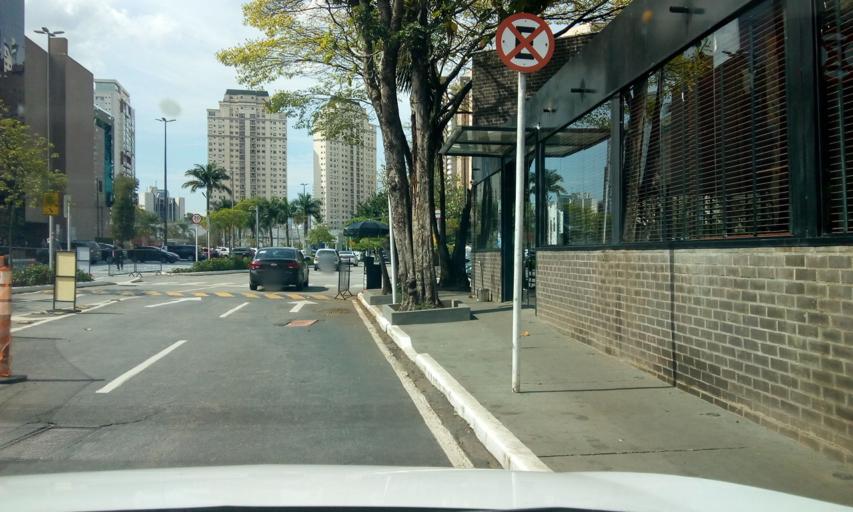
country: BR
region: Sao Paulo
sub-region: Taboao Da Serra
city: Taboao da Serra
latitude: -23.6240
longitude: -46.6979
